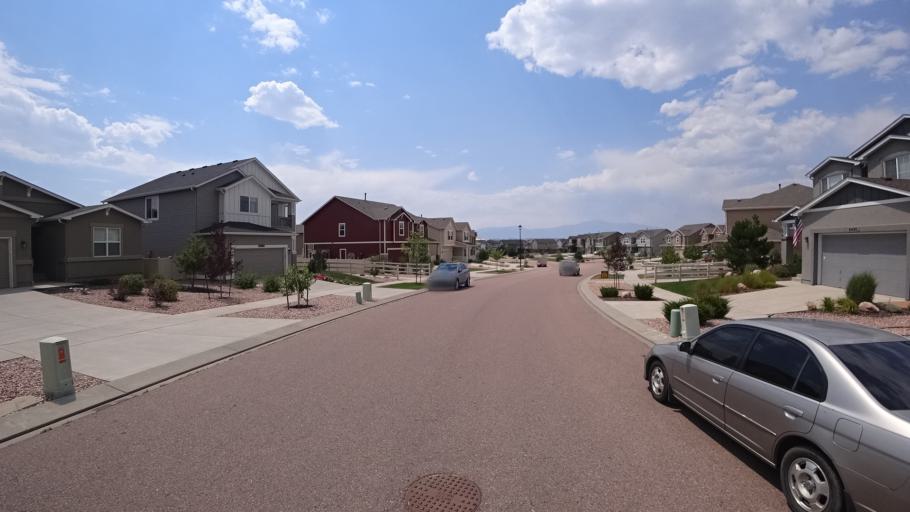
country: US
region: Colorado
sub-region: El Paso County
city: Black Forest
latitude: 38.9511
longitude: -104.6945
